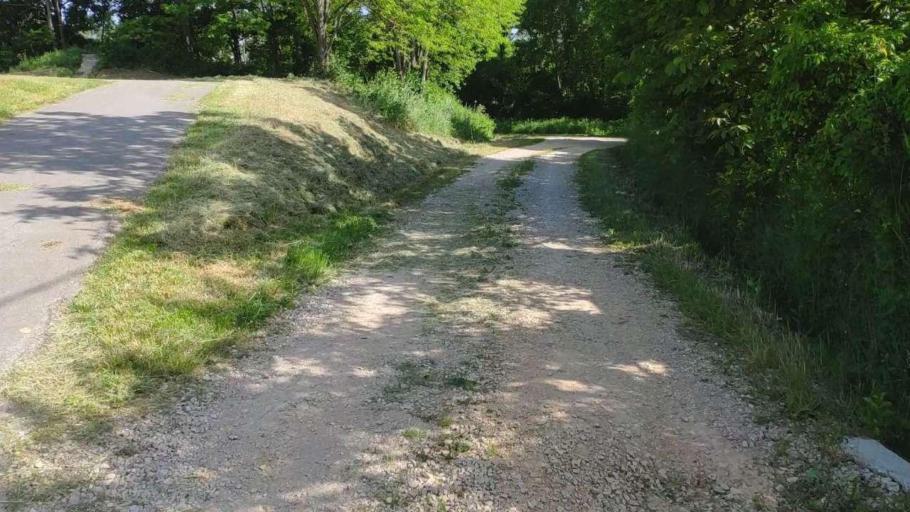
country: FR
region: Franche-Comte
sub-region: Departement du Jura
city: Bletterans
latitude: 46.7141
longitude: 5.4530
